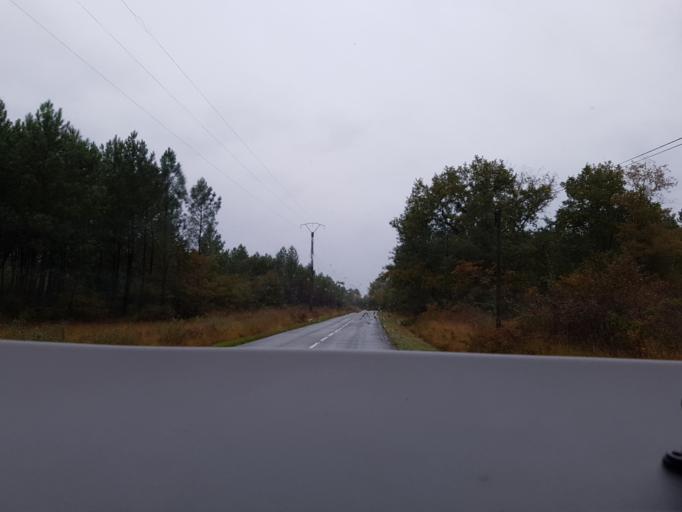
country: FR
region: Aquitaine
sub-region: Departement des Landes
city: Pissos
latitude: 44.3692
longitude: -0.6466
